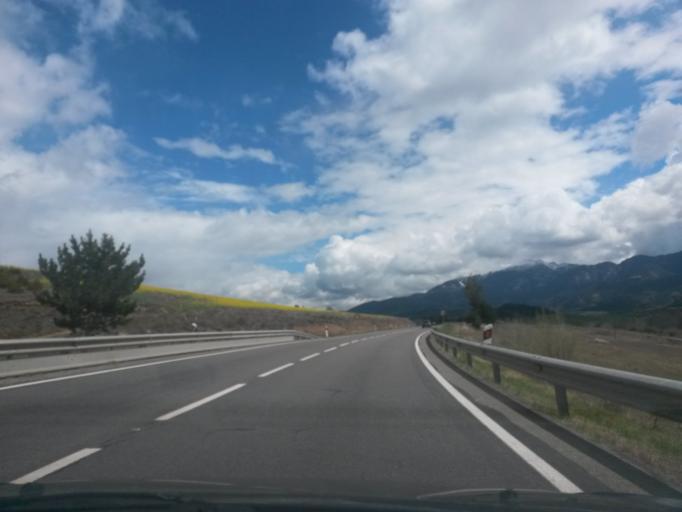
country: ES
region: Catalonia
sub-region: Provincia de Lleida
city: Bellver de Cerdanya
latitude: 42.3739
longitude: 1.7528
